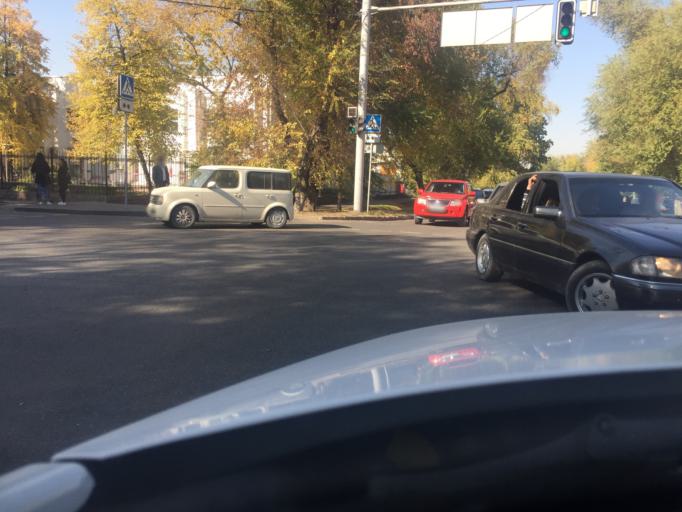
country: KZ
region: Almaty Qalasy
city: Almaty
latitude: 43.2575
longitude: 76.9109
